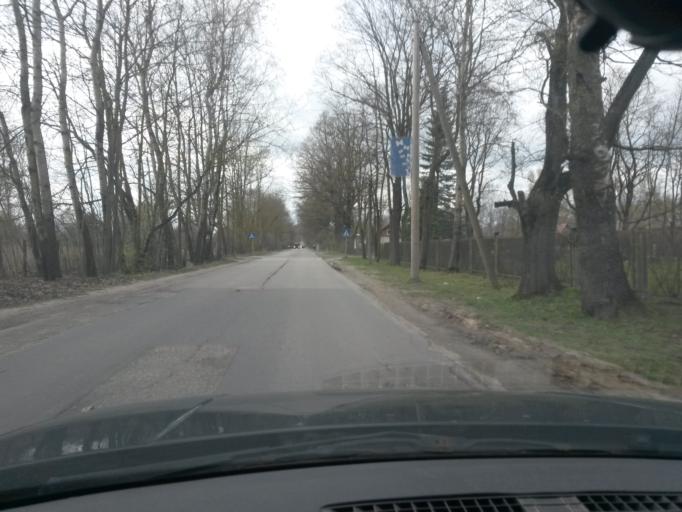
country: LV
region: Kekava
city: Kekava
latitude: 56.8943
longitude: 24.2384
